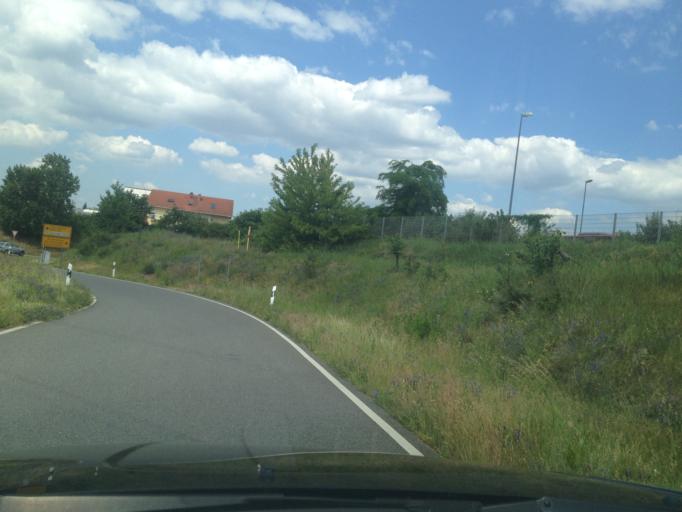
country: DE
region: Baden-Wuerttemberg
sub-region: Karlsruhe Region
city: Bruhl
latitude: 49.4007
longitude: 8.5610
